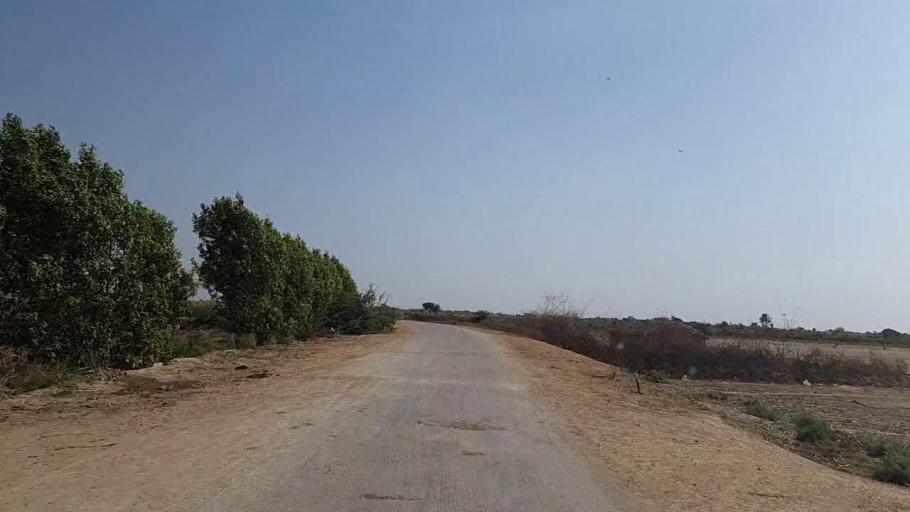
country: PK
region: Sindh
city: Daro Mehar
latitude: 24.7676
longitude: 68.1822
